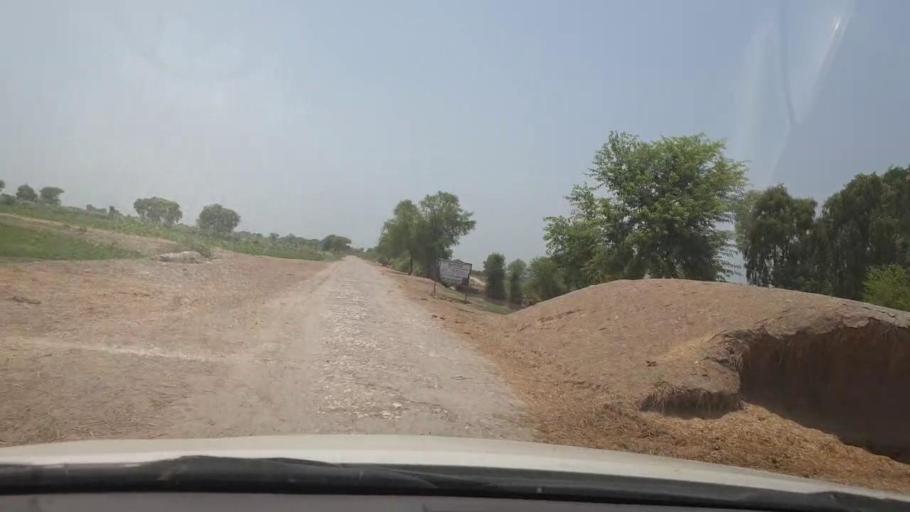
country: PK
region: Sindh
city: Shikarpur
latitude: 28.0870
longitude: 68.5618
